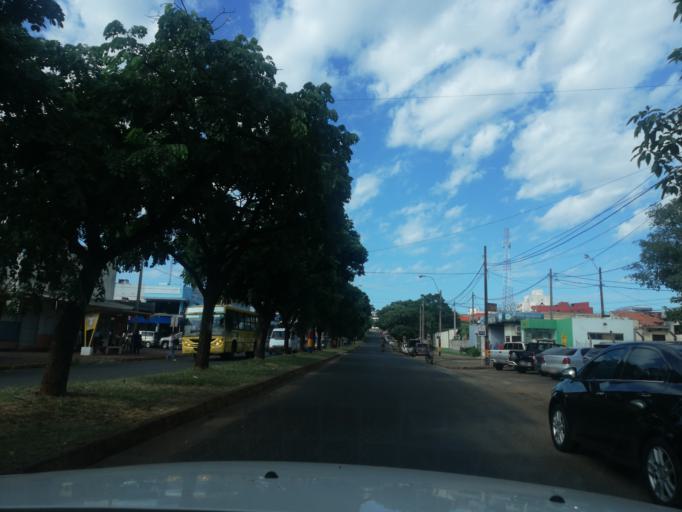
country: PY
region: Itapua
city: Encarnacion
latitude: -27.3556
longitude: -55.8476
